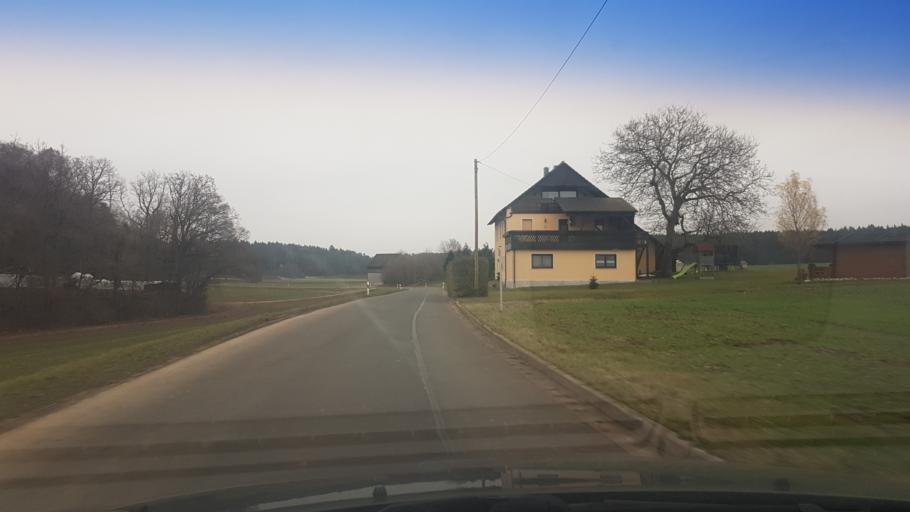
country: DE
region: Bavaria
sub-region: Upper Franconia
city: Stadelhofen
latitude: 50.0294
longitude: 11.2399
